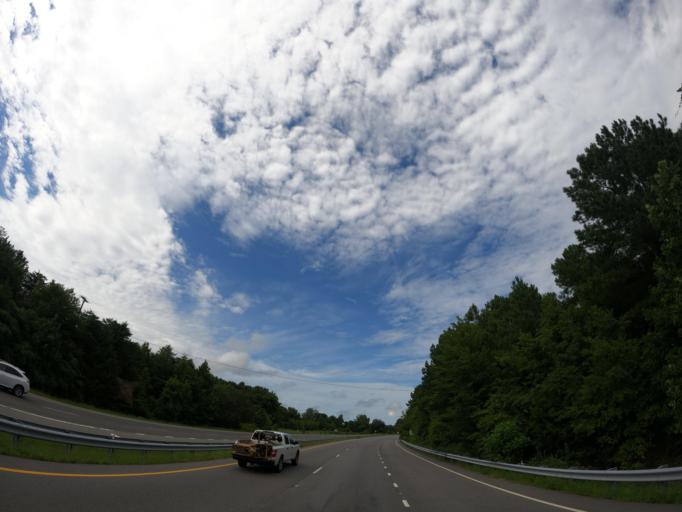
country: US
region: Maryland
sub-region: Calvert County
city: Chesapeake Ranch Estates
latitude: 38.3662
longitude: -76.4515
